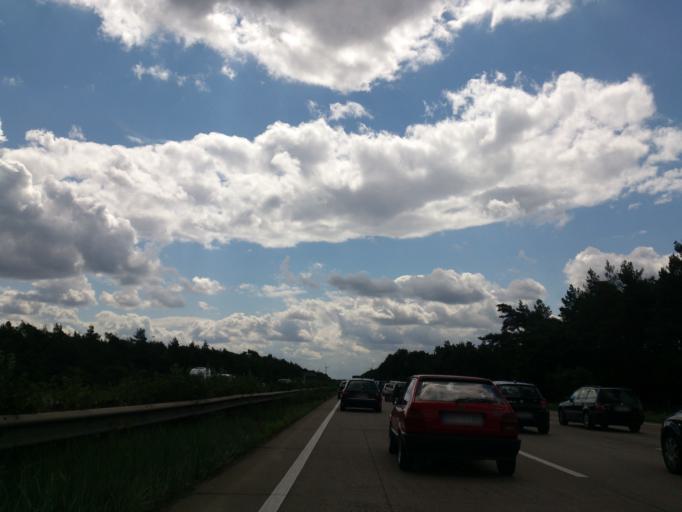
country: DE
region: Lower Saxony
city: Elze
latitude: 52.6093
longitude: 9.7388
